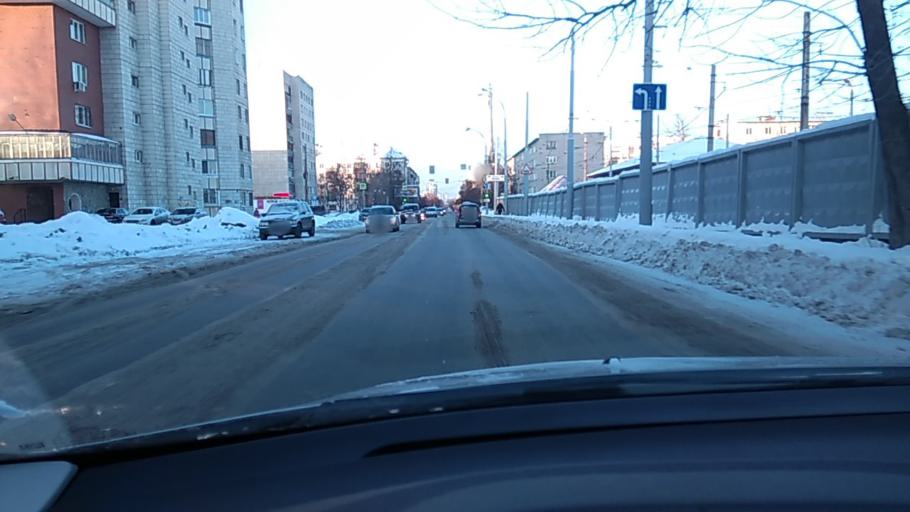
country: RU
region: Sverdlovsk
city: Yekaterinburg
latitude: 56.8125
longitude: 60.6117
